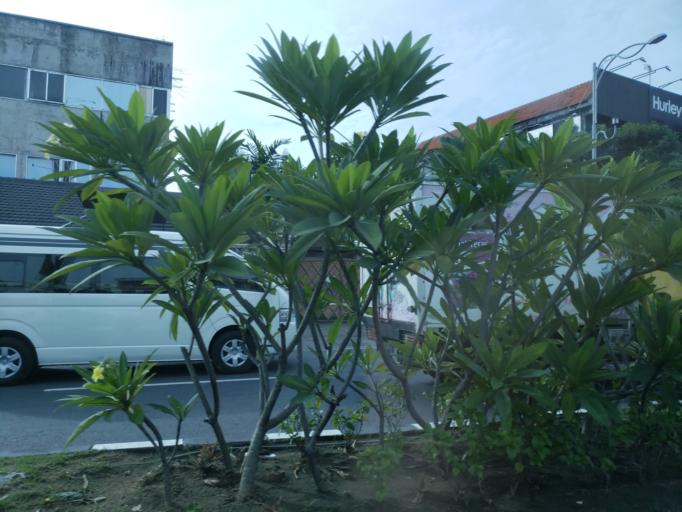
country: ID
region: Bali
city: Jabajero
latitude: -8.7255
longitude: 115.1809
